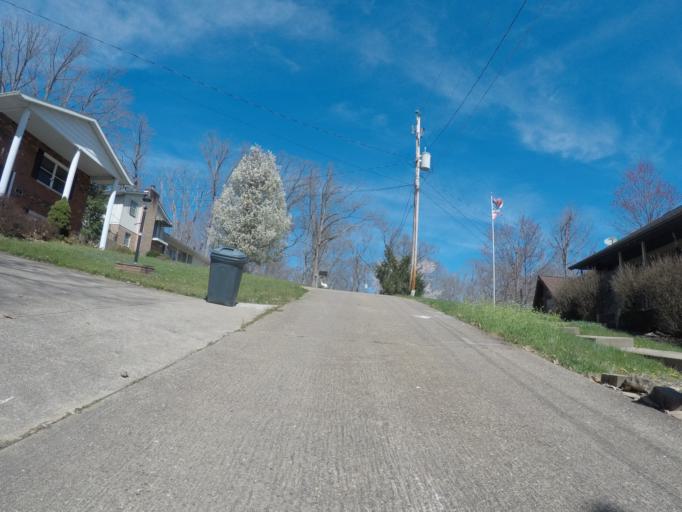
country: US
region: West Virginia
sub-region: Cabell County
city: Pea Ridge
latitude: 38.4024
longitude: -82.3374
